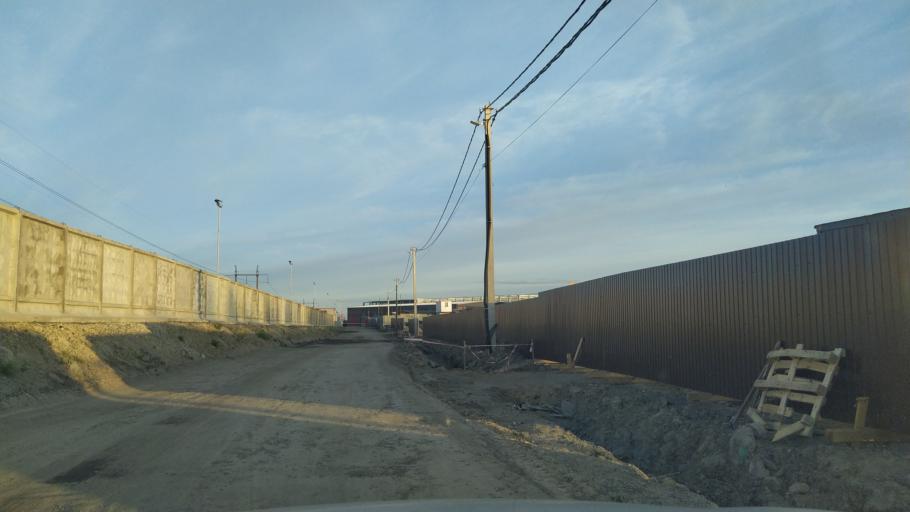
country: RU
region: St.-Petersburg
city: Obukhovo
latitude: 59.8041
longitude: 30.4598
